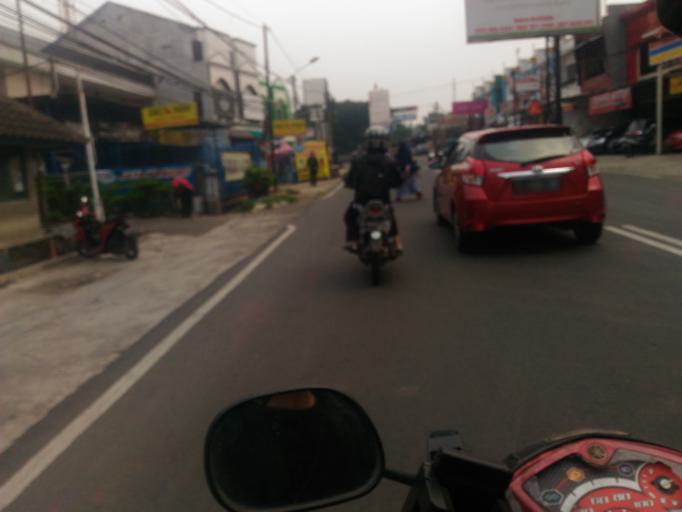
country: ID
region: West Java
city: Bogor
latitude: -6.6329
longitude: 106.8255
